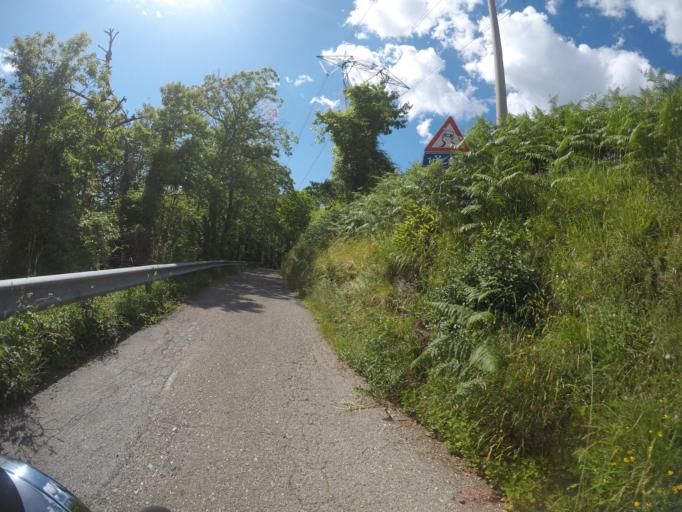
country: IT
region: Tuscany
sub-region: Provincia di Massa-Carrara
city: Casola in Lunigiana
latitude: 44.1774
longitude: 10.1802
